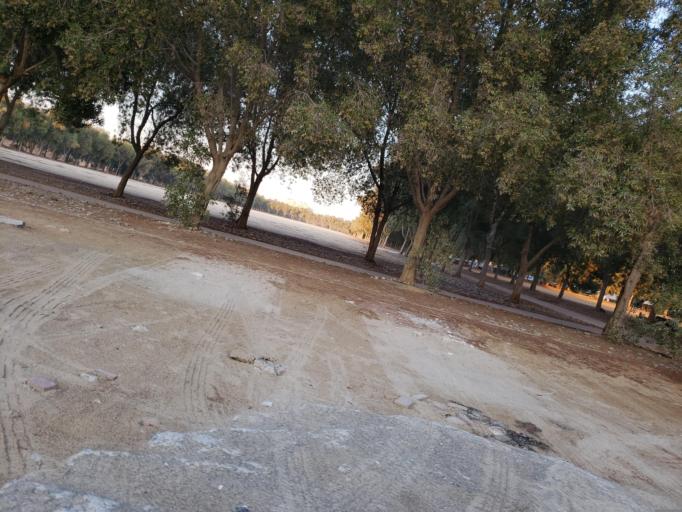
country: AE
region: Dubai
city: Dubai
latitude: 25.0055
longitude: 55.2455
